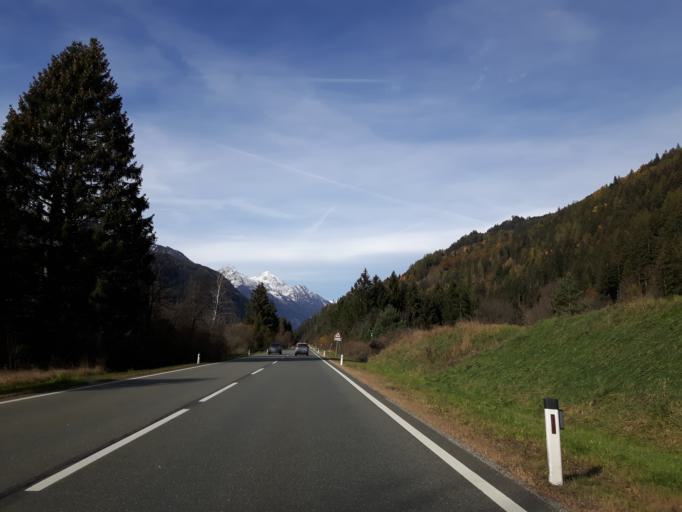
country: AT
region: Tyrol
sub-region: Politischer Bezirk Lienz
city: Schlaiten
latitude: 46.8741
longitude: 12.6780
